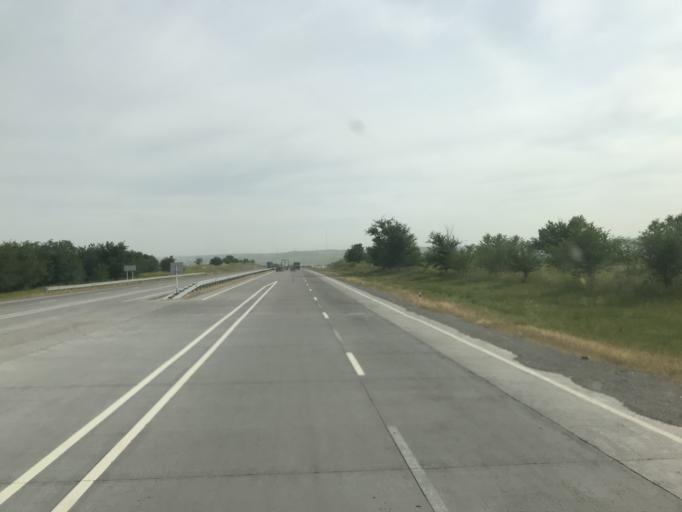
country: KZ
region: Ongtustik Qazaqstan
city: Shymkent
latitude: 42.1951
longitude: 69.5073
